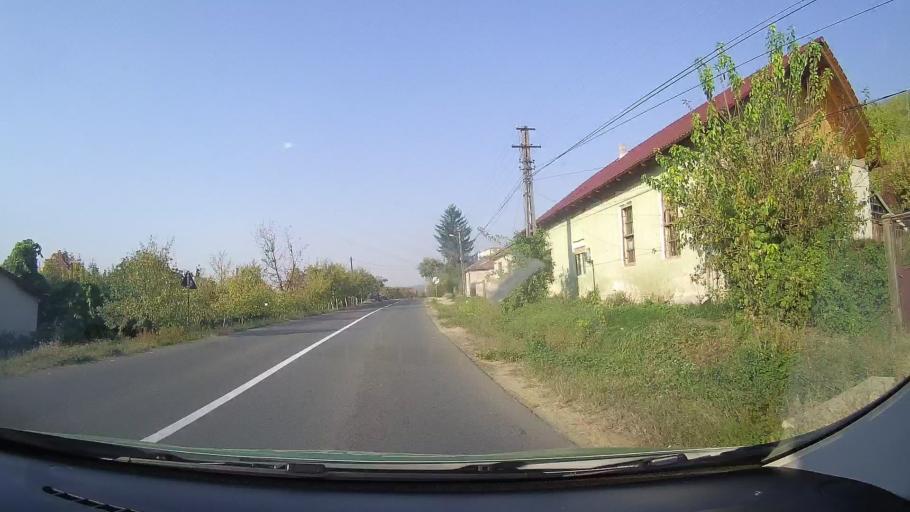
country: RO
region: Arad
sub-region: Comuna Paulis
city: Paulis
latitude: 46.1154
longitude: 21.5962
